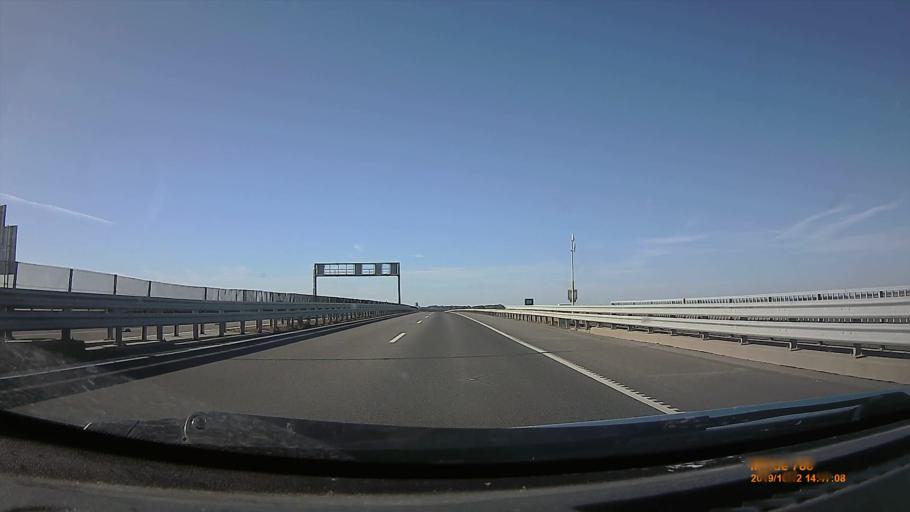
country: HU
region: Hajdu-Bihar
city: Berettyoujfalu
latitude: 47.2788
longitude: 21.5427
